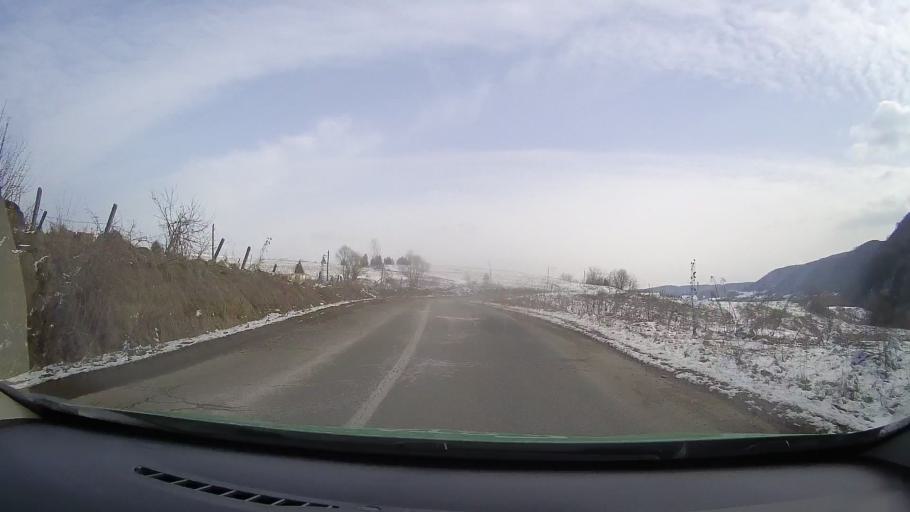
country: RO
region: Mures
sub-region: Comuna Apold
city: Saes
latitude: 46.1629
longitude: 24.7600
